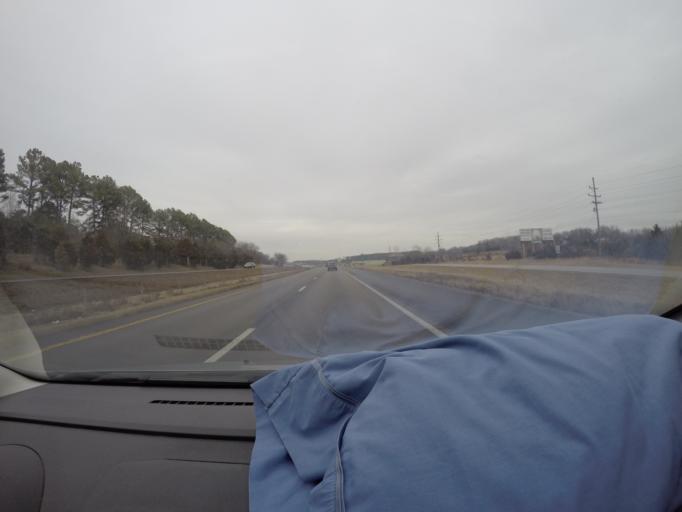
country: US
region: Missouri
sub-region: Warren County
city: Warrenton
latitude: 38.8195
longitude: -91.1701
